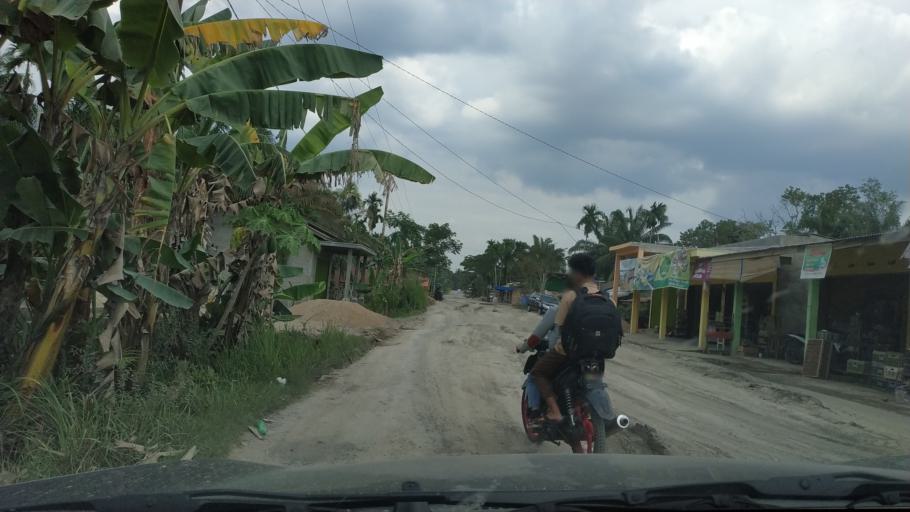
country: ID
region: Riau
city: Sungaisalak
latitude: -0.5648
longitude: 102.9623
